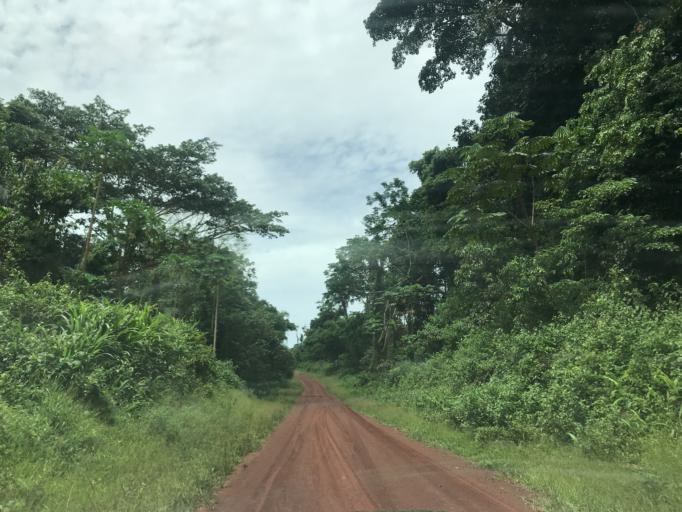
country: CD
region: Eastern Province
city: Buta
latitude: 2.4126
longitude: 24.8952
